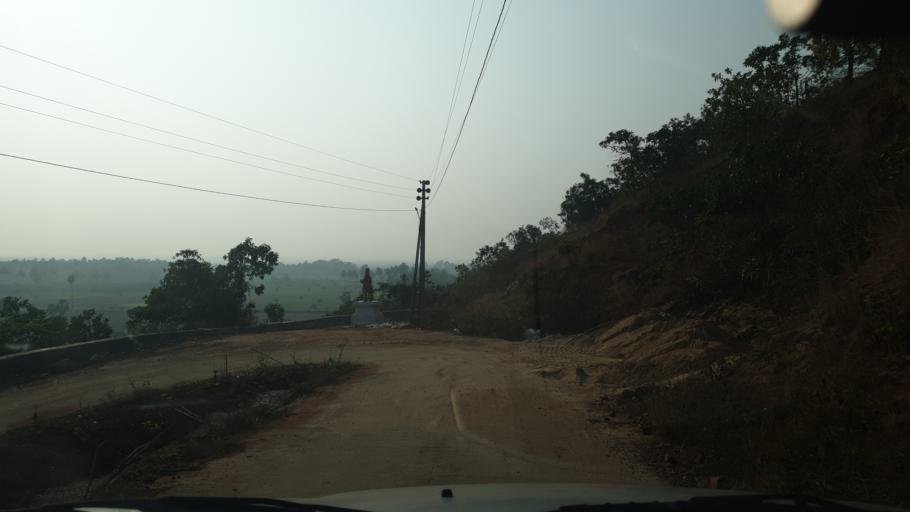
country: IN
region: Andhra Pradesh
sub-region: Srikakulam
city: Narasannapeta
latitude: 18.3314
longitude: 84.0341
